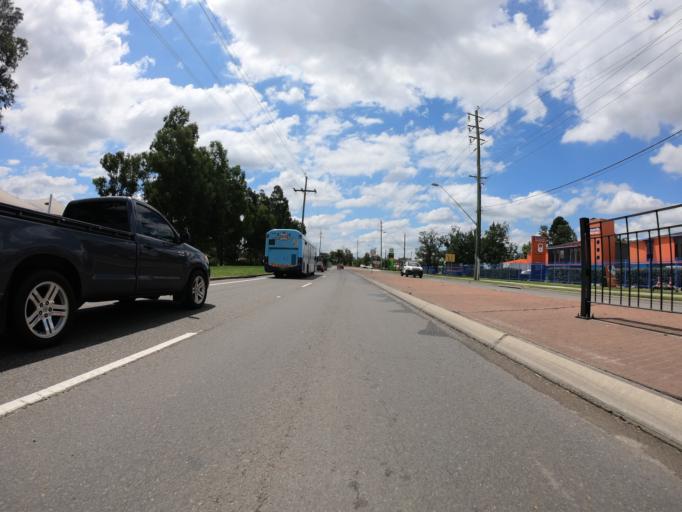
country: AU
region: New South Wales
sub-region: Penrith Municipality
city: Penrith
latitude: -33.7447
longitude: 150.6914
